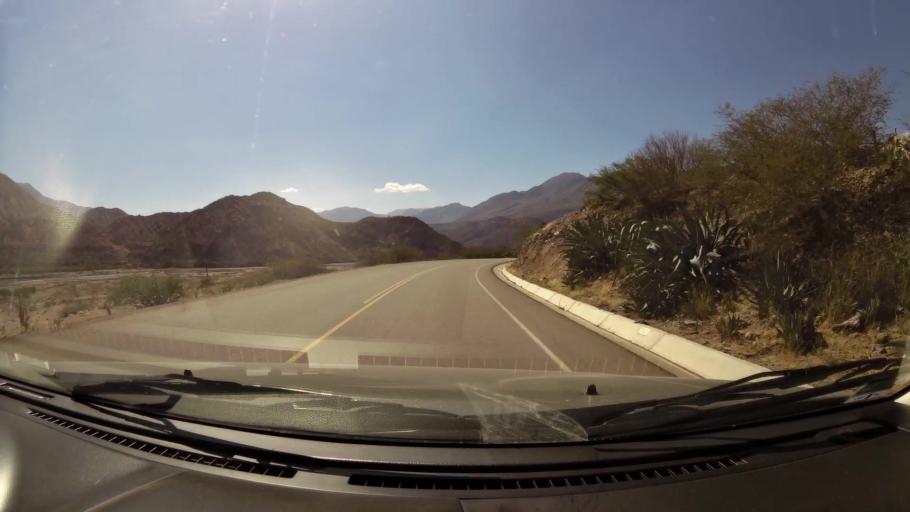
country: PE
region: Huancavelica
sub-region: Provincia de Acobamba
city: Marcas
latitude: -12.8622
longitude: -74.3302
